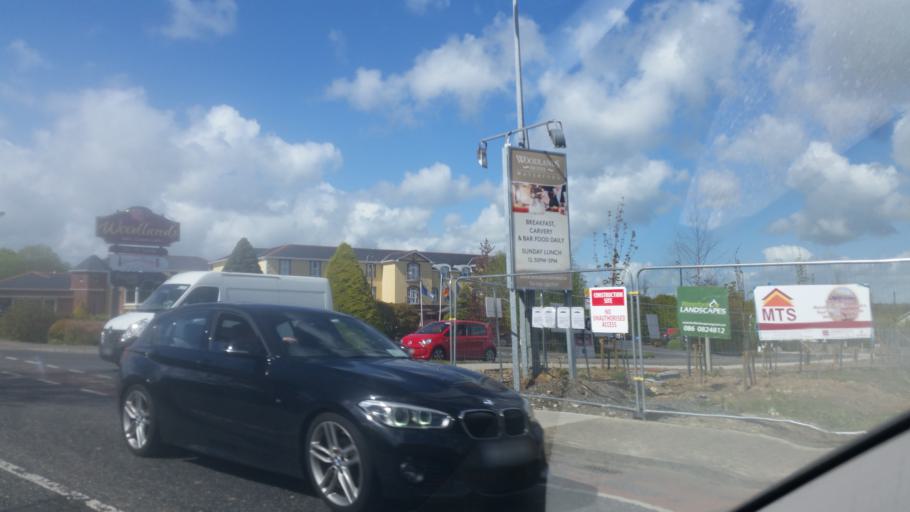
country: IE
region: Munster
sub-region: Waterford
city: Waterford
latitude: 52.2384
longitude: -7.0637
